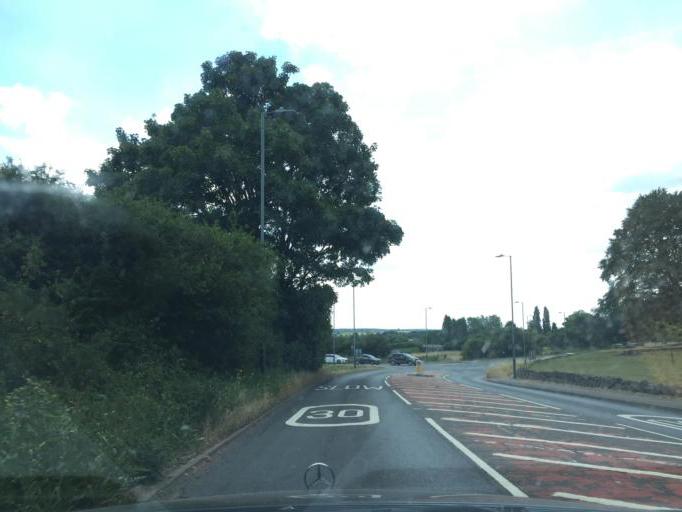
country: GB
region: England
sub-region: Warwickshire
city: Bedworth
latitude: 52.4503
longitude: -1.4096
